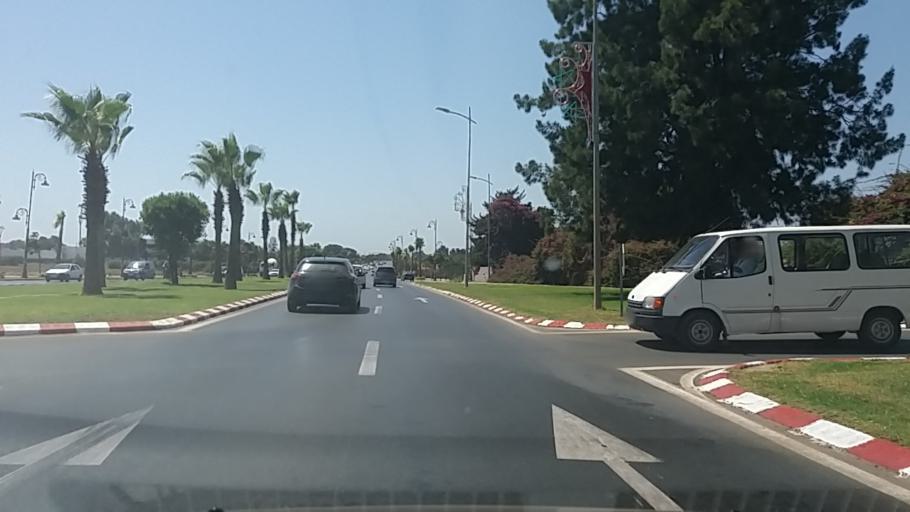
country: MA
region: Rabat-Sale-Zemmour-Zaer
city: Sale
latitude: 34.0311
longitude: -6.7544
